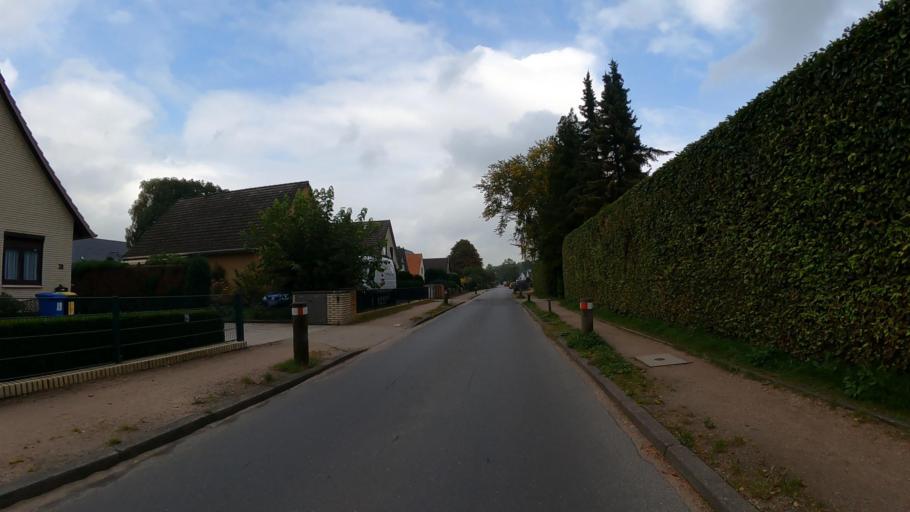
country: DE
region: Schleswig-Holstein
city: Halstenbek
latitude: 53.6100
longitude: 9.8685
